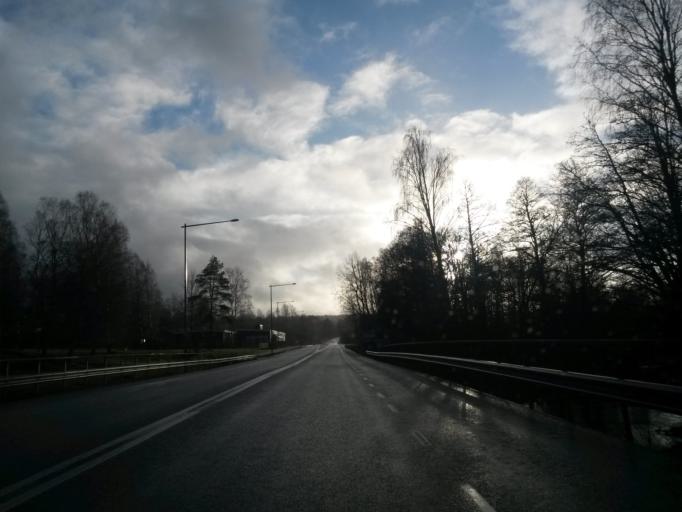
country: SE
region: Vaestra Goetaland
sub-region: Boras Kommun
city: Ganghester
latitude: 57.8066
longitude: 13.0113
